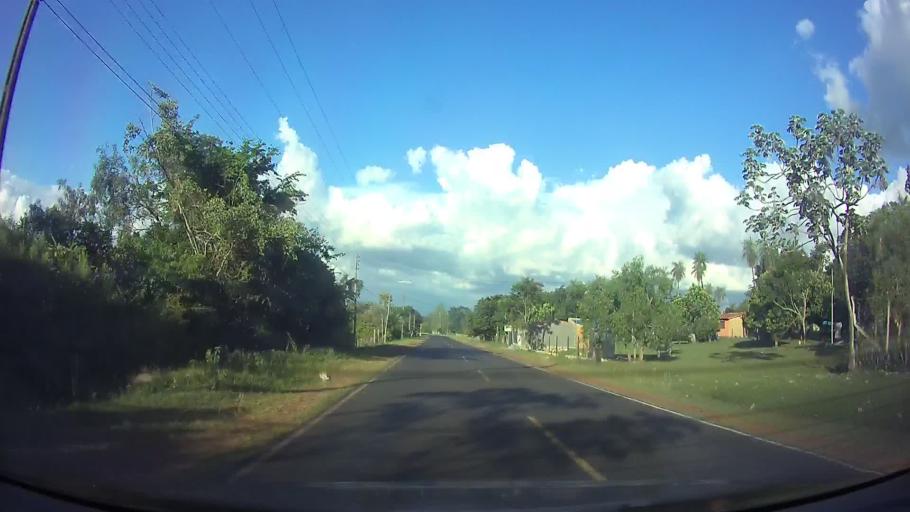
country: PY
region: Cordillera
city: Emboscada
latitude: -25.1693
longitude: -57.2758
